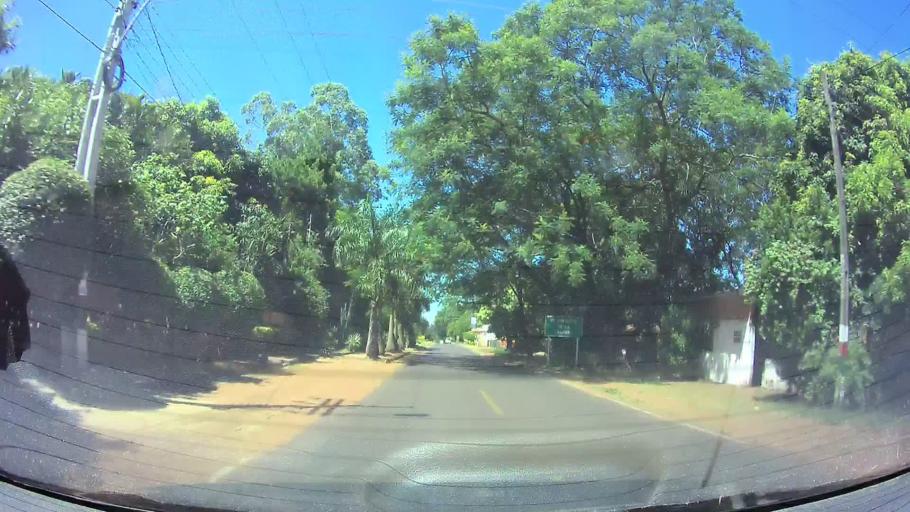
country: PY
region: Central
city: Aregua
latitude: -25.2939
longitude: -57.4132
